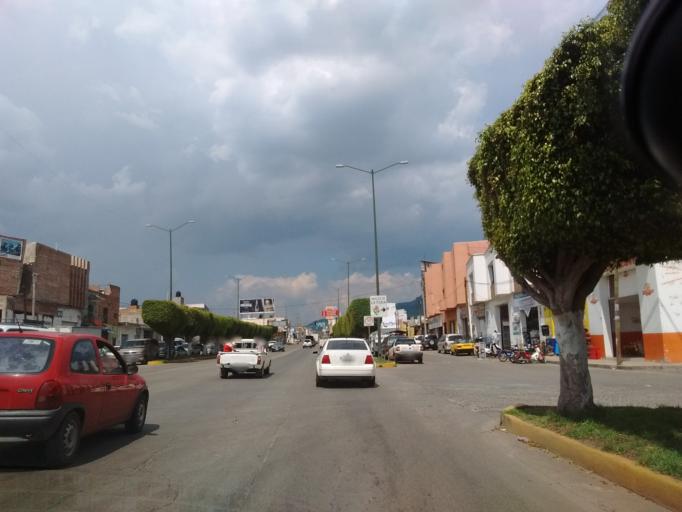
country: MX
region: Jalisco
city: Atotonilco el Alto
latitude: 20.5446
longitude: -102.5113
